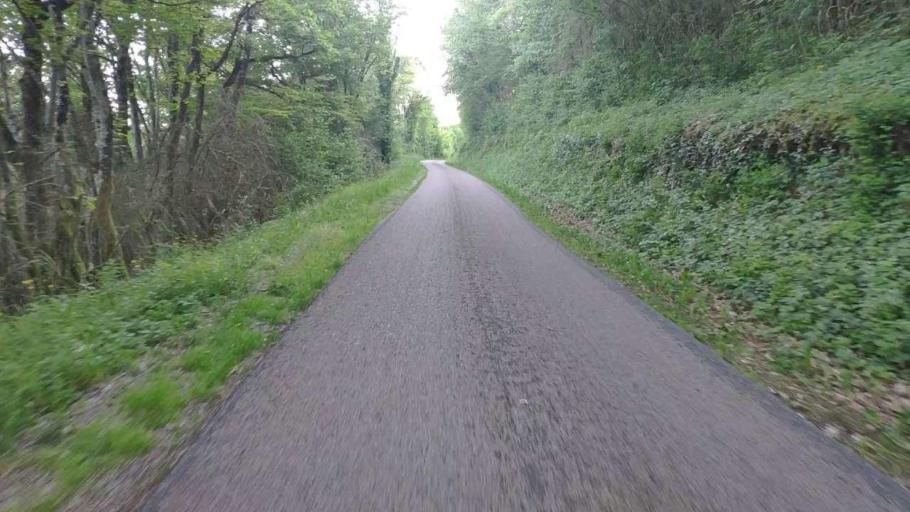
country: FR
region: Franche-Comte
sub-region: Departement du Jura
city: Perrigny
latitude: 46.7168
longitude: 5.6035
